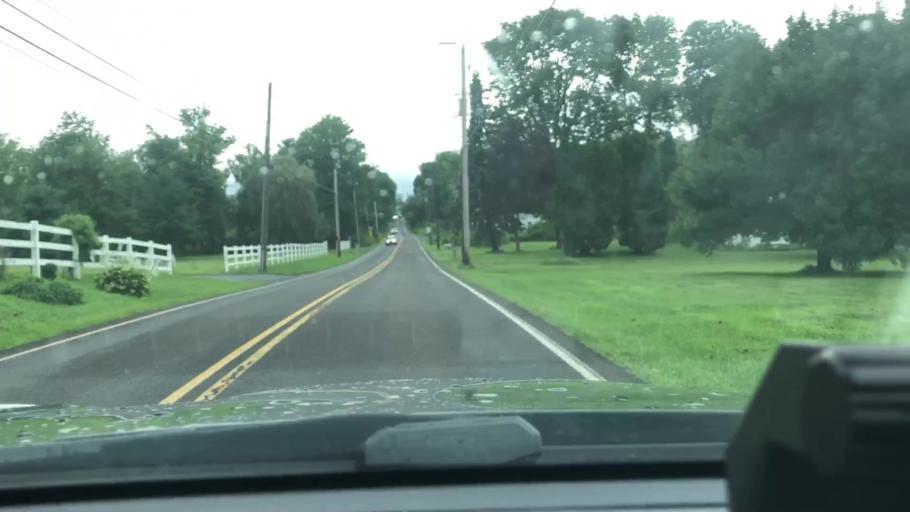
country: US
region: Pennsylvania
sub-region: Lehigh County
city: Coopersburg
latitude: 40.4936
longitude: -75.3946
